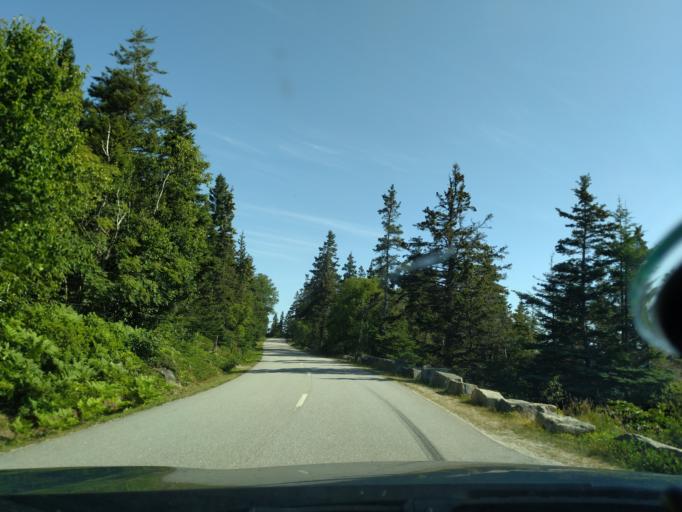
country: US
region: Maine
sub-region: Hancock County
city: Gouldsboro
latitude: 44.3398
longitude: -68.0450
